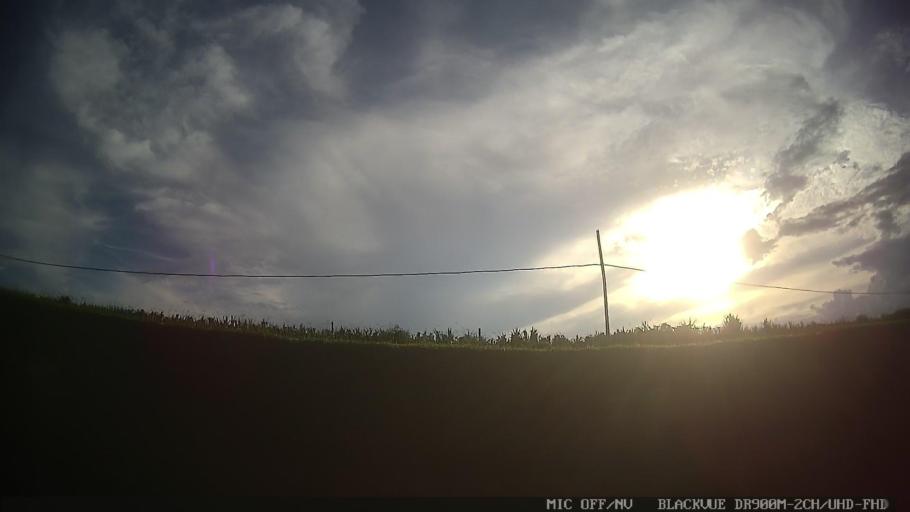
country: BR
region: Sao Paulo
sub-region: Tiete
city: Tiete
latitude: -23.1498
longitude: -47.6652
